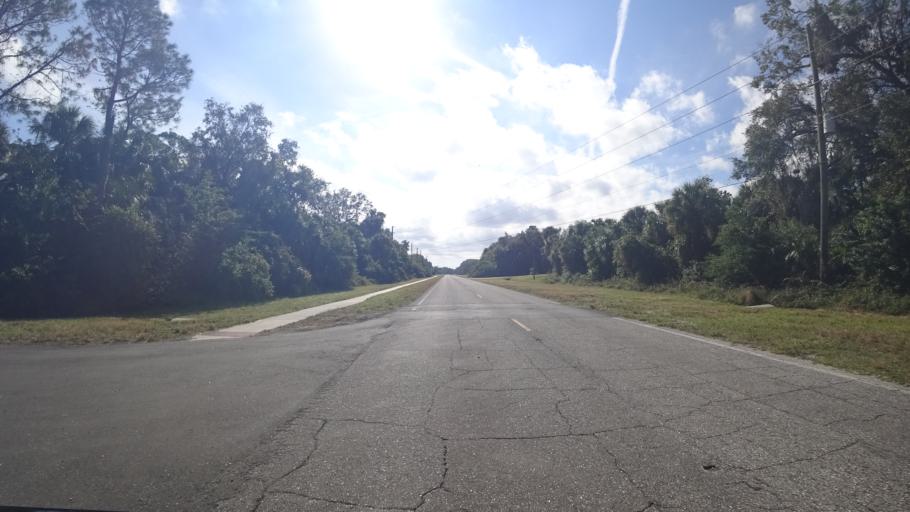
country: US
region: Florida
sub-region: Charlotte County
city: Port Charlotte
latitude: 27.0619
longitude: -82.1164
